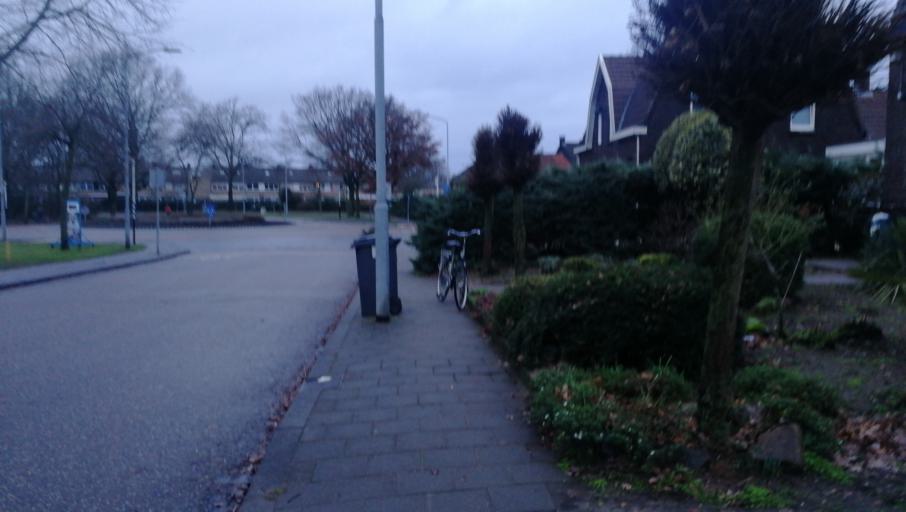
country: NL
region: Limburg
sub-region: Gemeente Venlo
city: Tegelen
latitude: 51.3597
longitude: 6.1412
